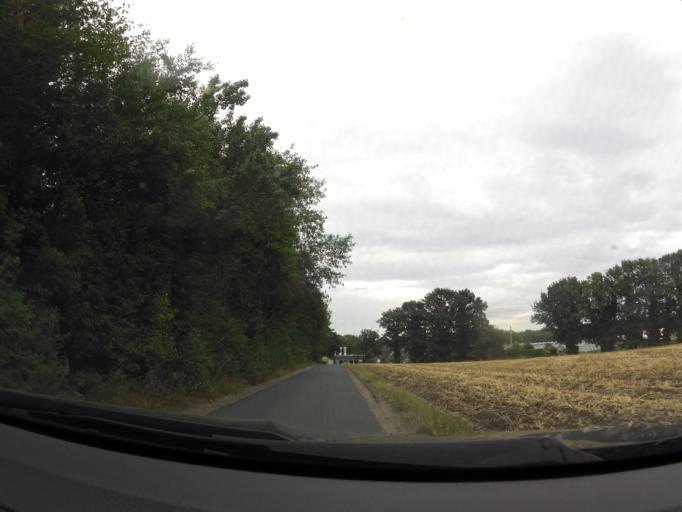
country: DE
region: North Rhine-Westphalia
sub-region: Regierungsbezirk Dusseldorf
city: Kevelaer
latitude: 51.5468
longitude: 6.2184
